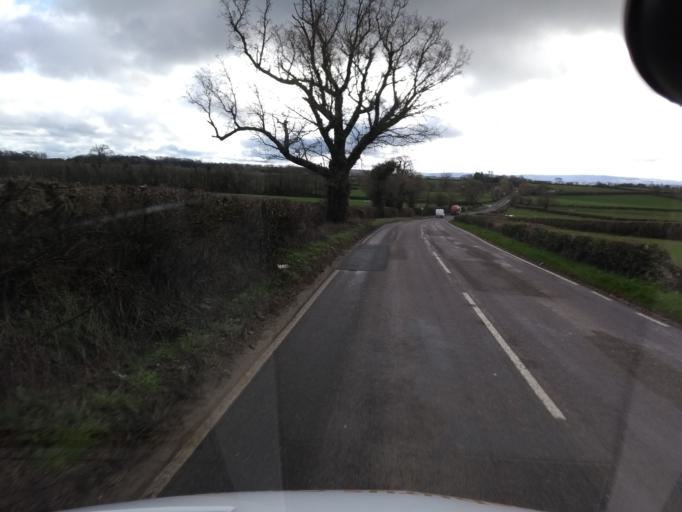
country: GB
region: England
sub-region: Dorset
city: Sherborne
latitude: 50.9311
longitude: -2.4996
